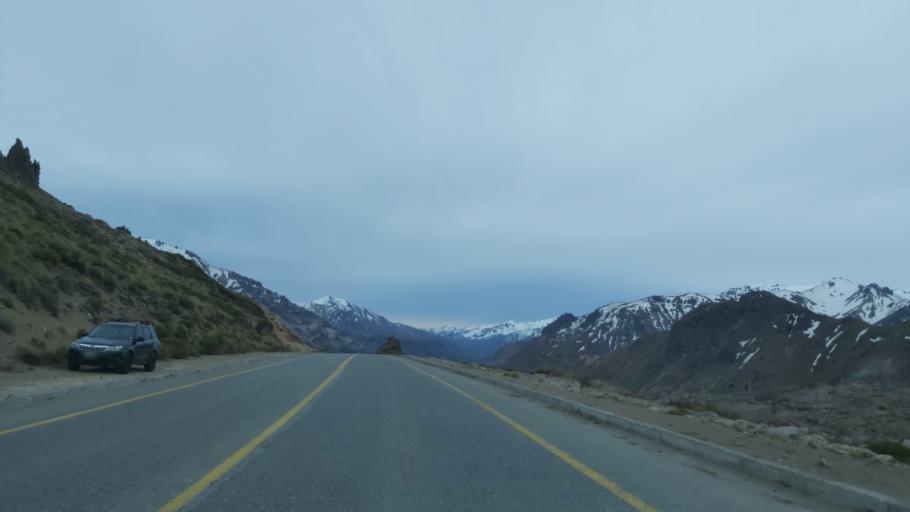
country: CL
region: Maule
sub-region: Provincia de Linares
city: Colbun
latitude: -35.9574
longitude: -70.5743
